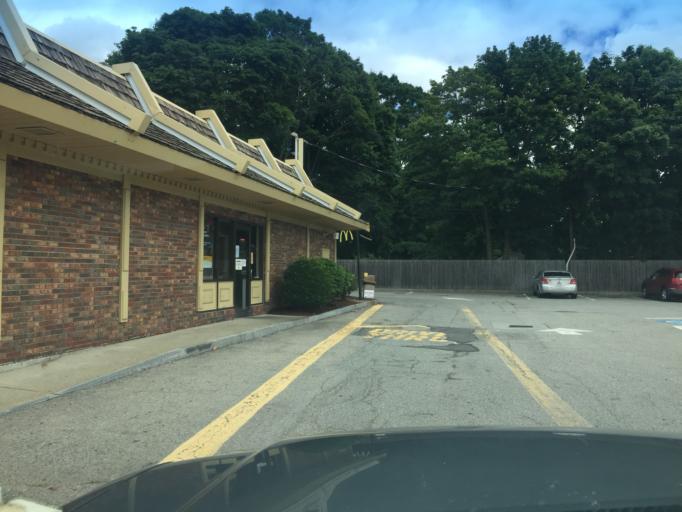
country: US
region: Massachusetts
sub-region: Middlesex County
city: Reading
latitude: 42.5205
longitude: -71.1031
